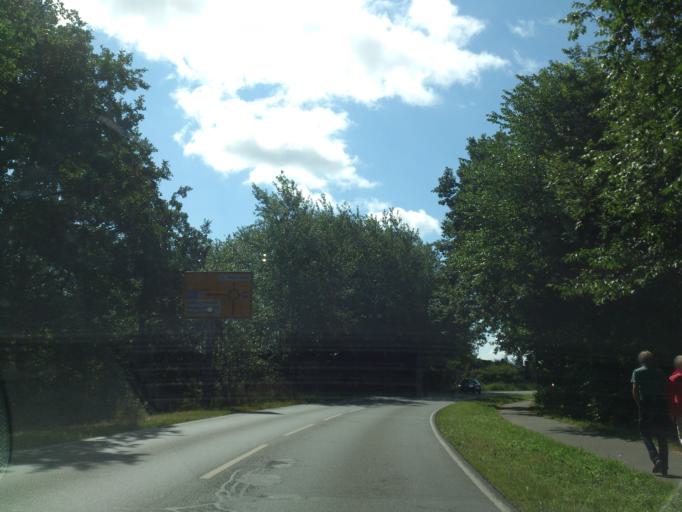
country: DE
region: Schleswig-Holstein
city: Sankt Peter-Ording
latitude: 54.3037
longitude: 8.6498
